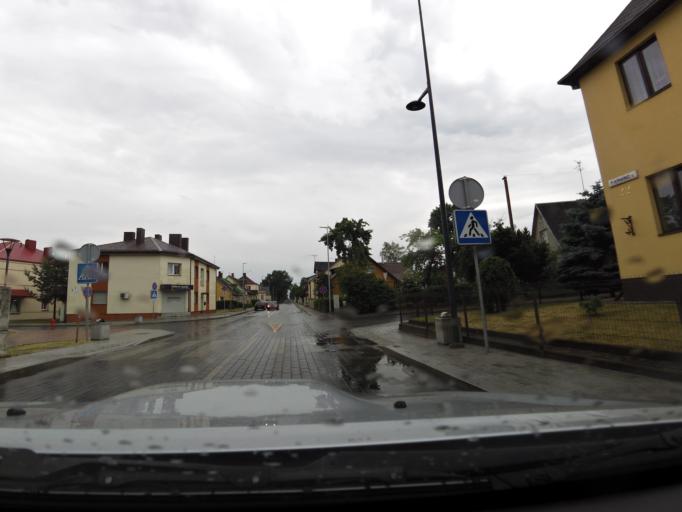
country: LT
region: Marijampoles apskritis
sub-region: Marijampole Municipality
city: Marijampole
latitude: 54.5521
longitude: 23.3452
